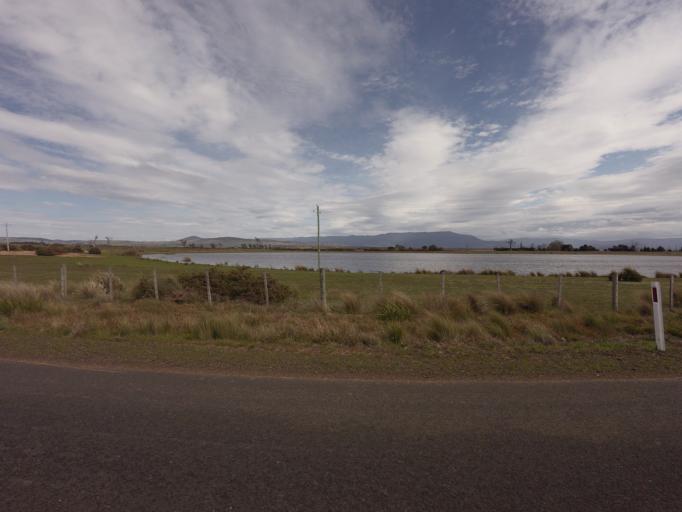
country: AU
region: Tasmania
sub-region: Northern Midlands
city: Evandale
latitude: -41.8281
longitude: 147.3234
